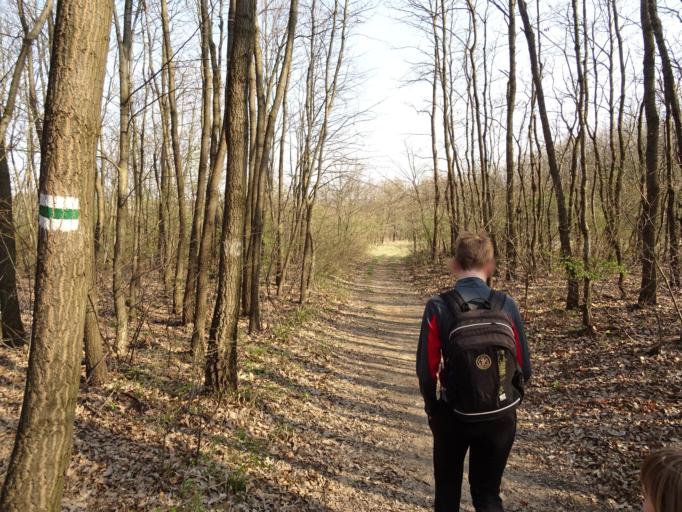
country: HU
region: Fejer
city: Csakvar
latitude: 47.4020
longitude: 18.4113
